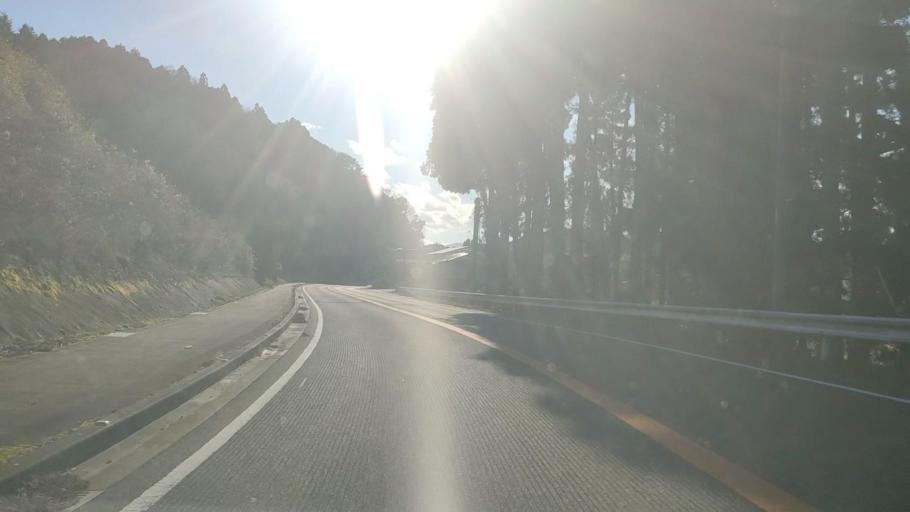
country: JP
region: Fukuoka
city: Maebaru-chuo
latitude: 33.4408
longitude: 130.2670
